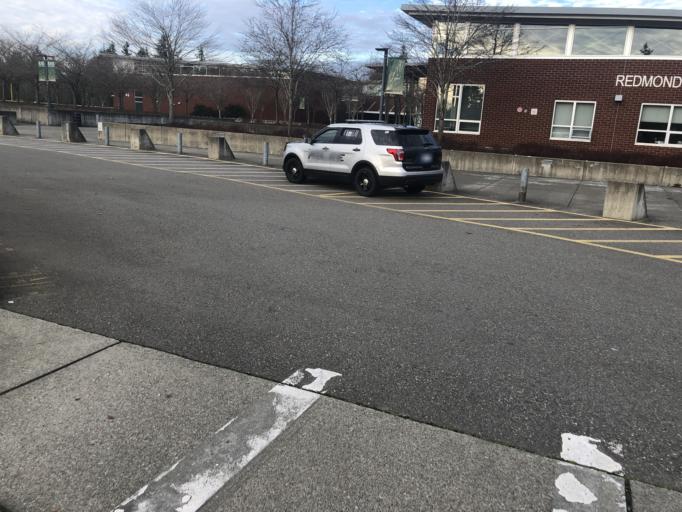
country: US
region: Washington
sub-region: King County
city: Redmond
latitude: 47.6947
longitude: -122.1071
